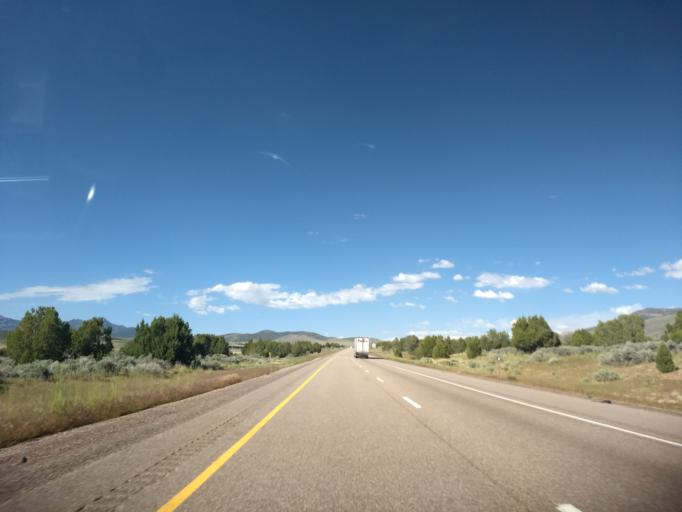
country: US
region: Utah
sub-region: Millard County
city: Fillmore
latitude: 39.1535
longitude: -112.2294
